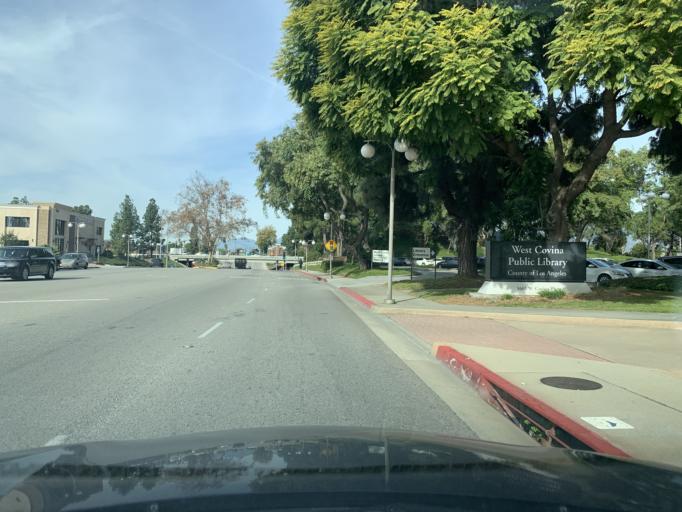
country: US
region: California
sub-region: Los Angeles County
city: West Covina
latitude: 34.0708
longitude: -117.9408
